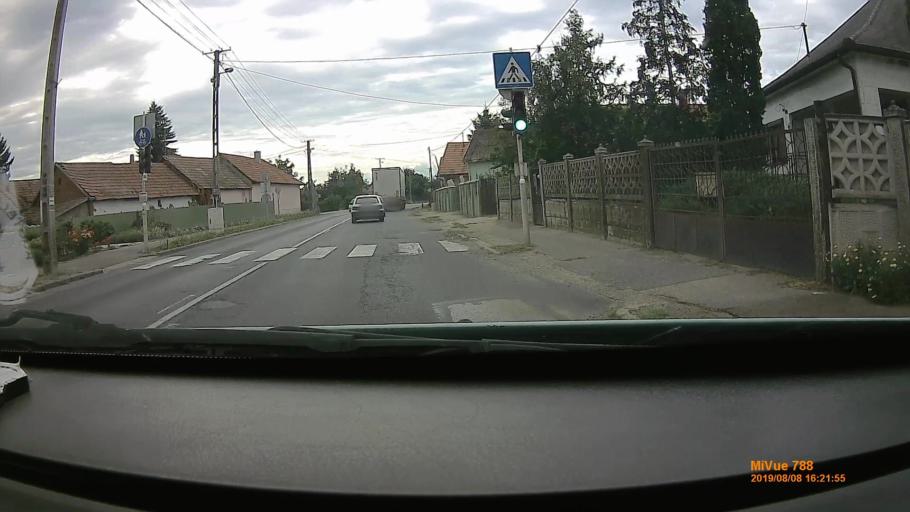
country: HU
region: Szabolcs-Szatmar-Bereg
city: Nyirmeggyes
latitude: 47.9700
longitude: 22.2547
